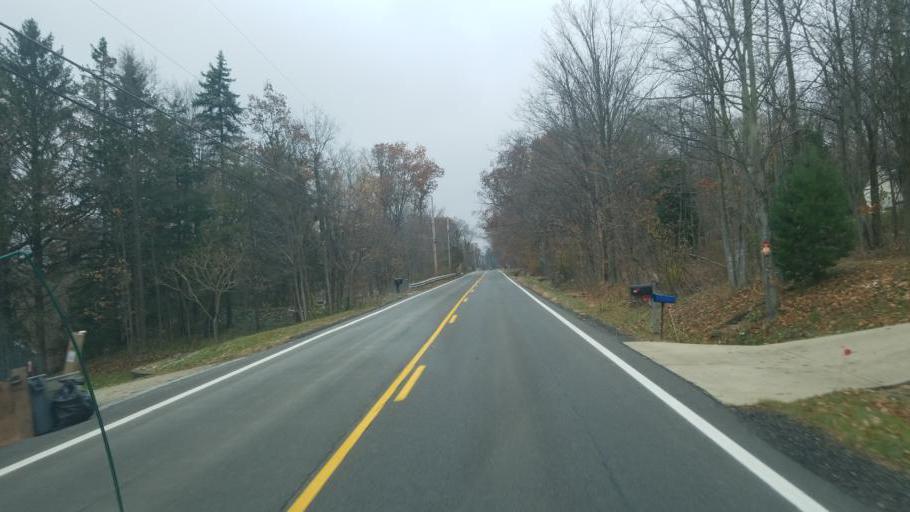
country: US
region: Ohio
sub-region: Cuyahoga County
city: North Royalton
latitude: 41.2674
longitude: -81.7252
